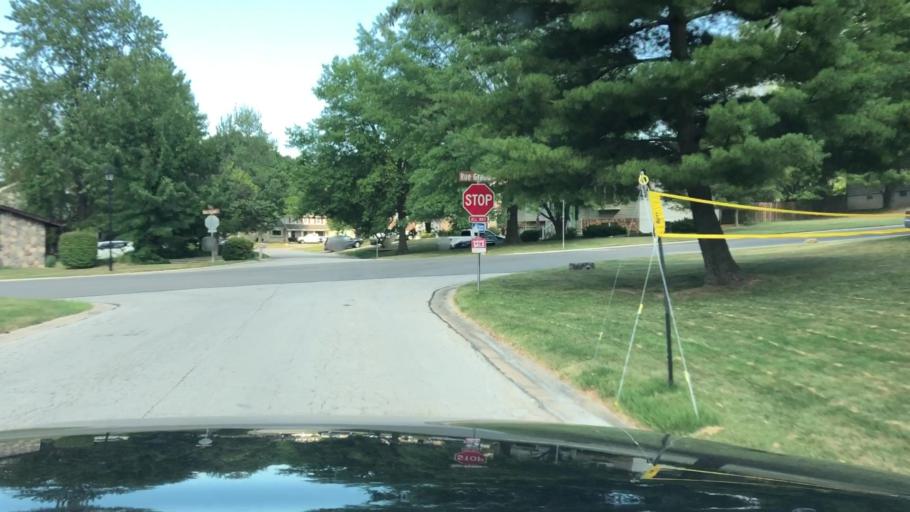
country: US
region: Missouri
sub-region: Saint Charles County
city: Lake Saint Louis
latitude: 38.7960
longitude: -90.8039
